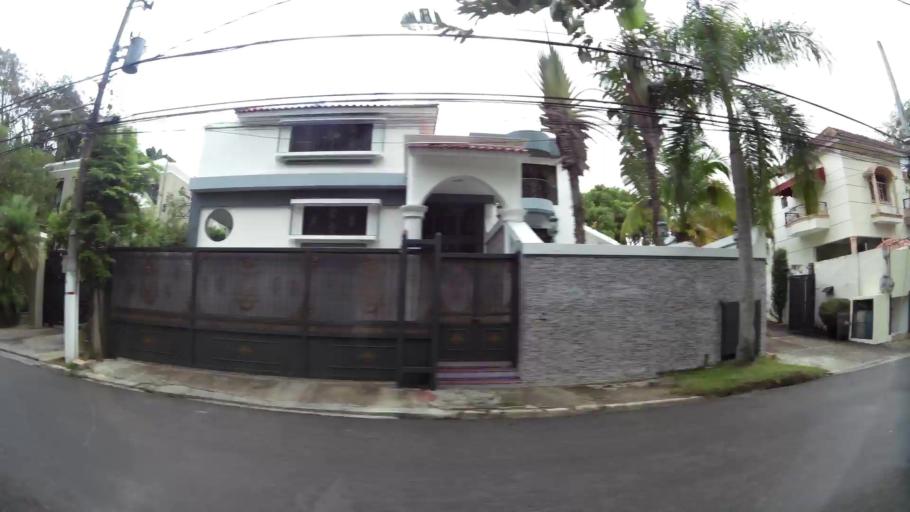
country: DO
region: Nacional
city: La Agustina
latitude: 18.5098
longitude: -69.9484
